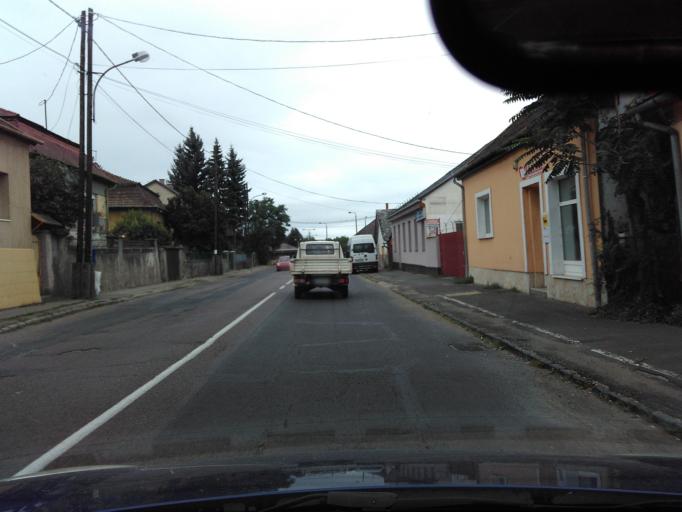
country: HU
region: Nograd
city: Salgotarjan
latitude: 48.0893
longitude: 19.7942
